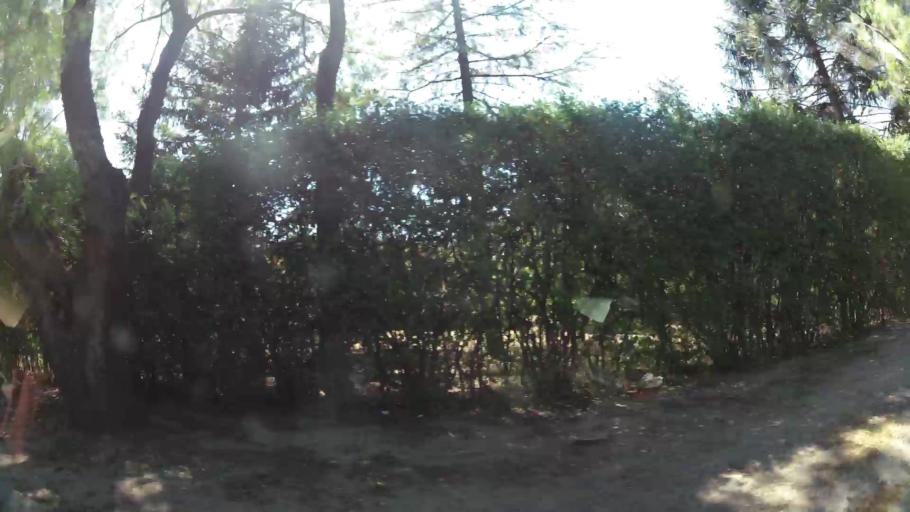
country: AR
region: Cordoba
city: Villa Allende
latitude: -31.2916
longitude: -64.2826
